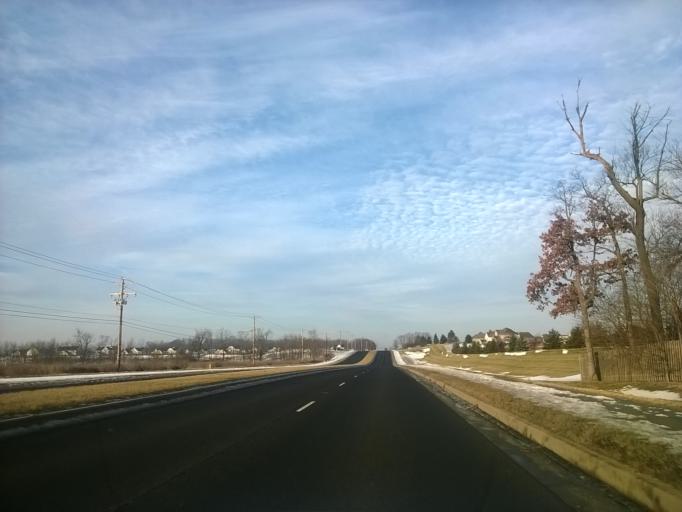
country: US
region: Indiana
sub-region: Hamilton County
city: Fishers
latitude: 40.0004
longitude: -86.0478
